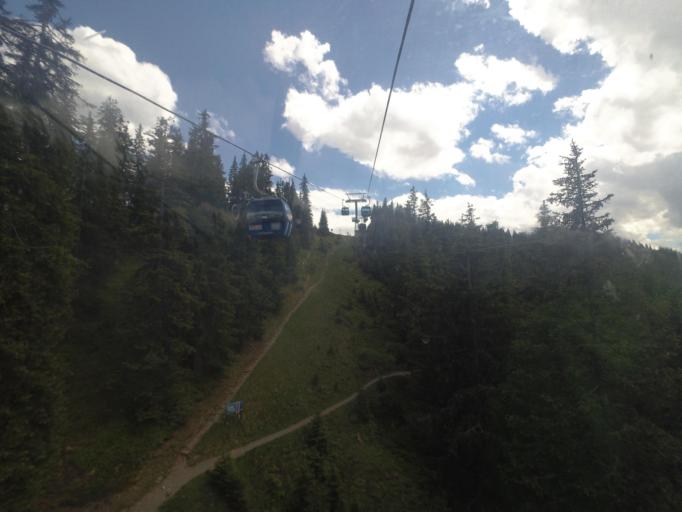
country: AT
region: Salzburg
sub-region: Politischer Bezirk Zell am See
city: Viehhofen
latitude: 47.4136
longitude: 12.7144
